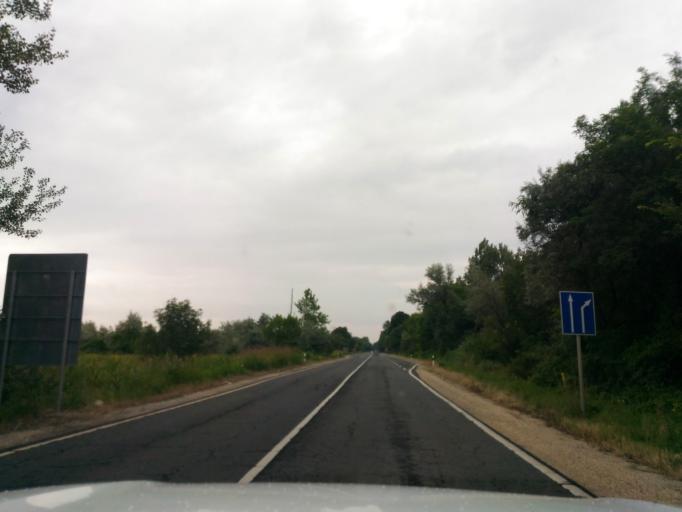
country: HU
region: Pest
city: Ocsa
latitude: 47.2827
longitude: 19.1967
